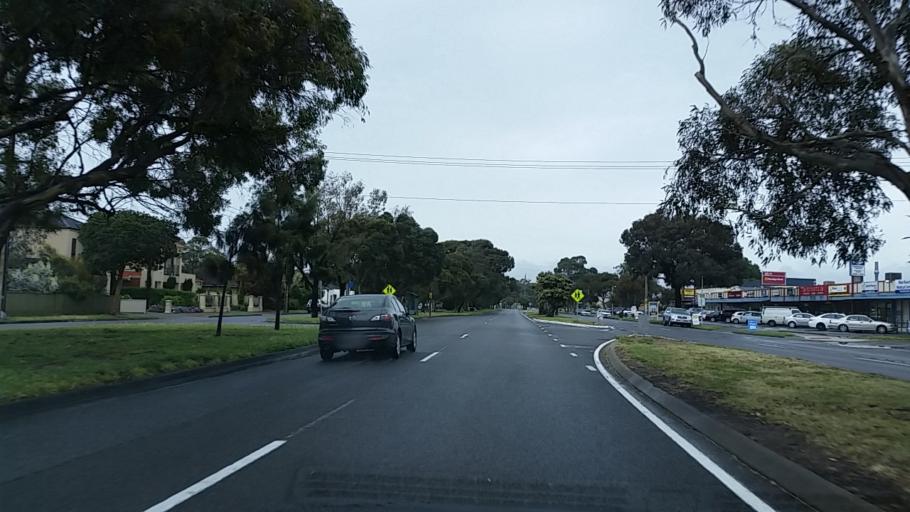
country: AU
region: South Australia
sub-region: Charles Sturt
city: Henley Beach
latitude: -34.9369
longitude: 138.5041
